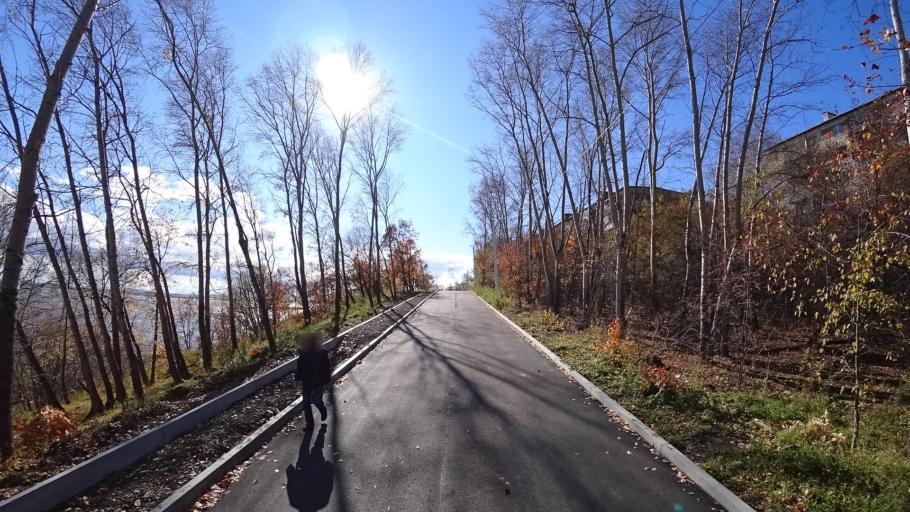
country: RU
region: Khabarovsk Krai
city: Amursk
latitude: 50.2161
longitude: 136.9067
